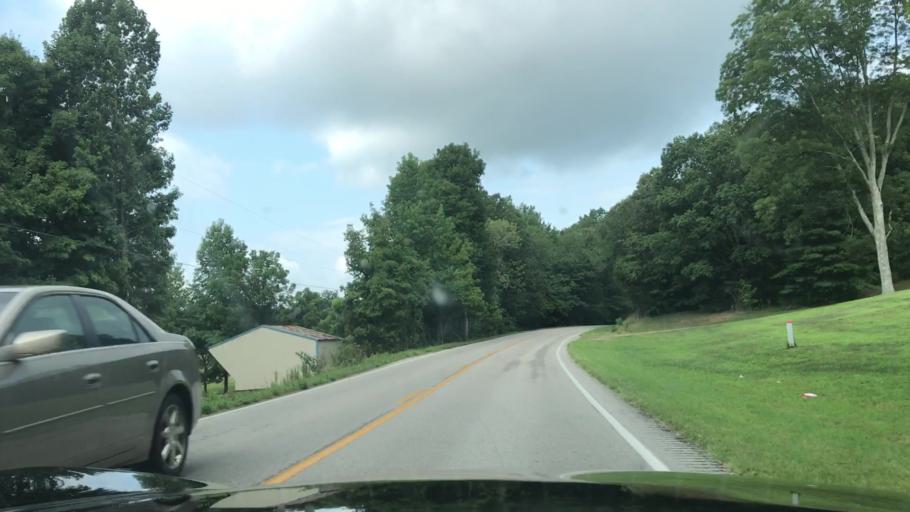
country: US
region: Kentucky
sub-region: Butler County
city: Morgantown
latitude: 37.1727
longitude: -86.8342
